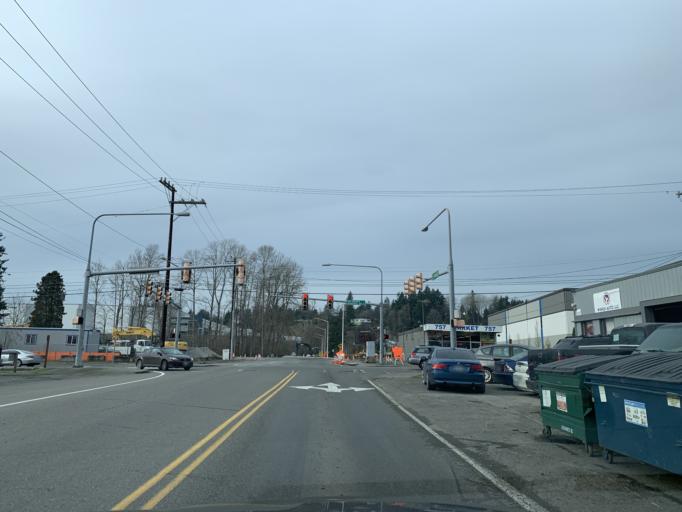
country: US
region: Washington
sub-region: King County
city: Boulevard Park
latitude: 47.4741
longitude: -122.3148
